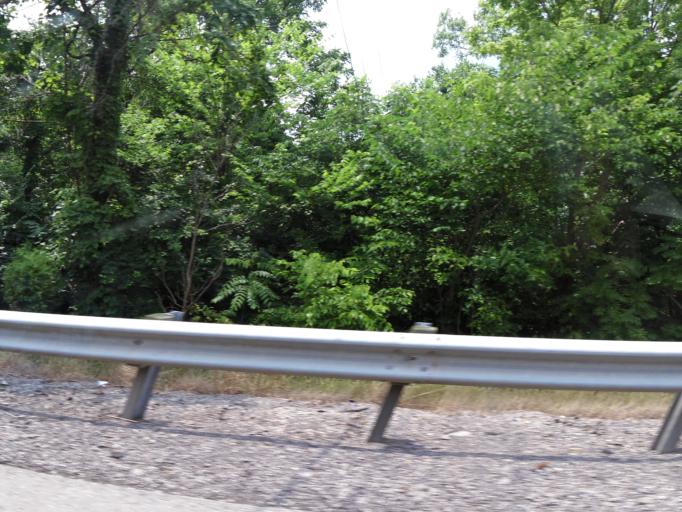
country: US
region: Kentucky
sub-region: Trimble County
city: Providence
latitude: 38.4817
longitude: -85.2673
